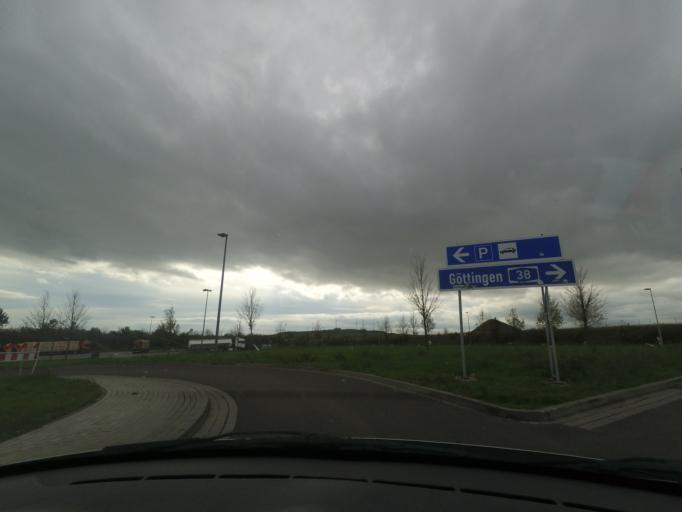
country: DE
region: Saxony-Anhalt
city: Allstedt
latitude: 51.4353
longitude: 11.4246
